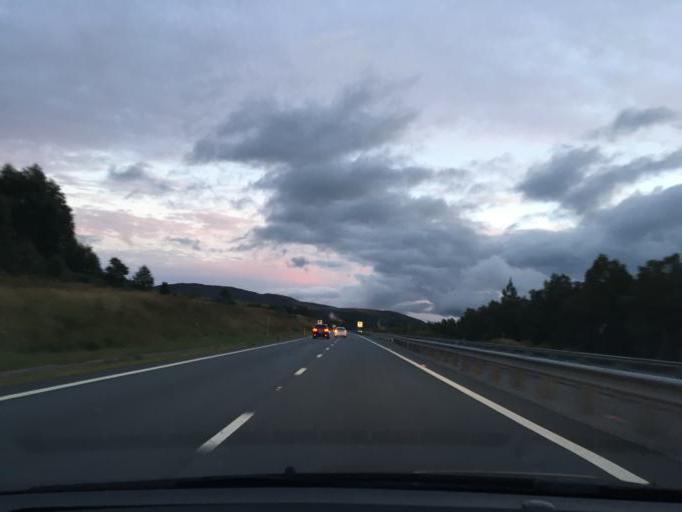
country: GB
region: Scotland
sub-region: Highland
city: Kingussie
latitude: 57.0219
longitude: -4.1594
